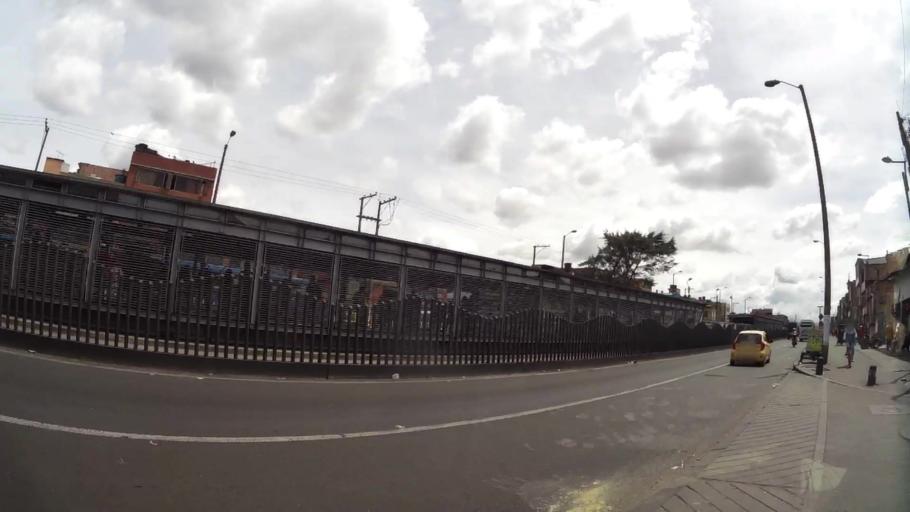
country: CO
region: Cundinamarca
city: Soacha
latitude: 4.6341
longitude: -74.1637
